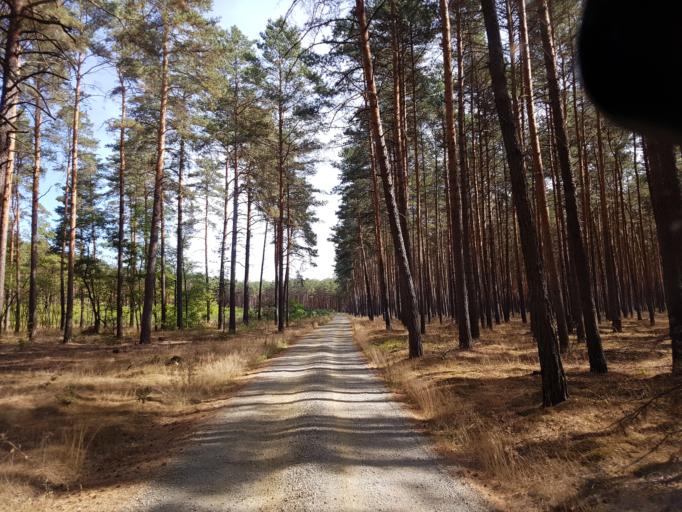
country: DE
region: Brandenburg
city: Sonnewalde
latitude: 51.7607
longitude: 13.6552
